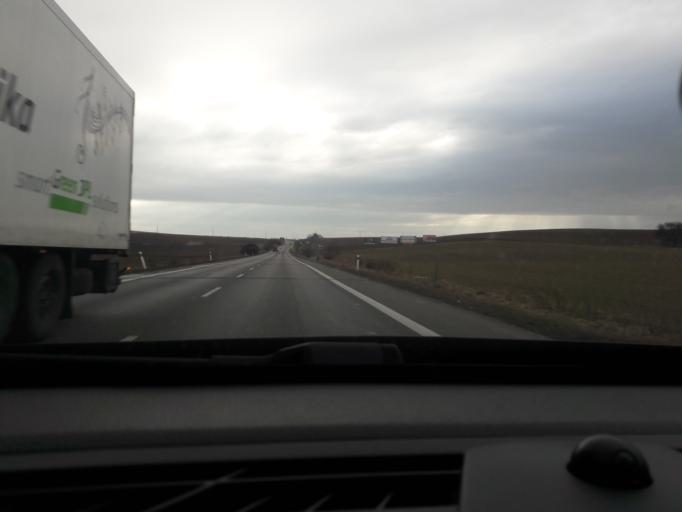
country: SK
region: Banskobystricky
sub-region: Okres Banska Bystrica
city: Zvolen
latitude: 48.5676
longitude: 19.2291
